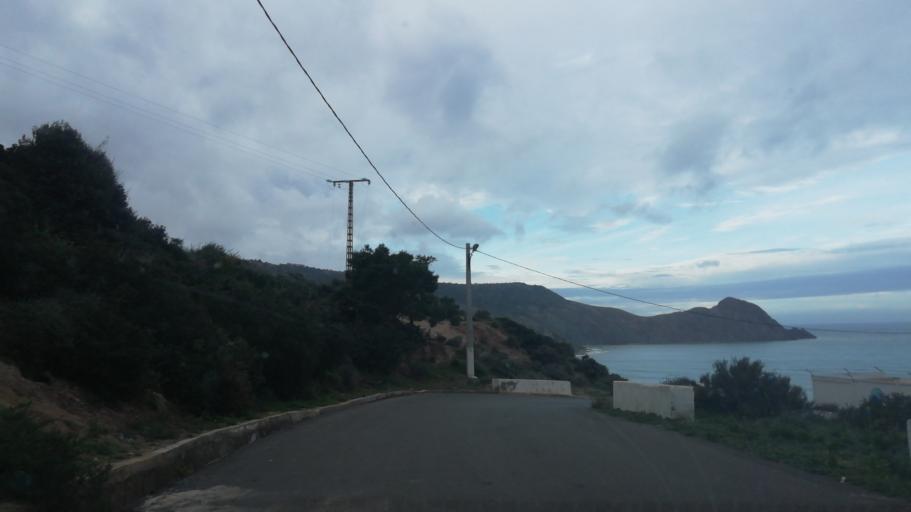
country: DZ
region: Oran
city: Bir el Djir
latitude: 35.7676
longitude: -0.5263
